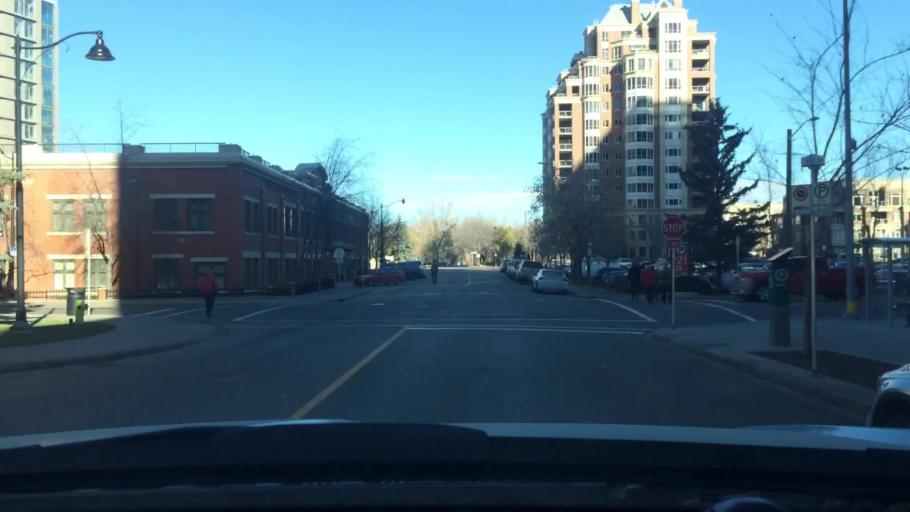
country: CA
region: Alberta
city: Calgary
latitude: 51.0513
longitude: -114.0760
